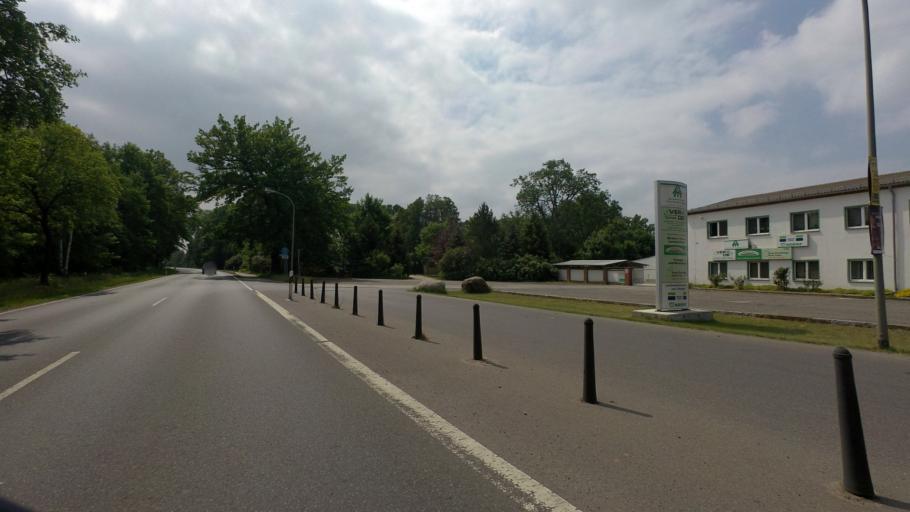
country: DE
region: Brandenburg
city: Drehnow
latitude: 51.8751
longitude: 14.3766
